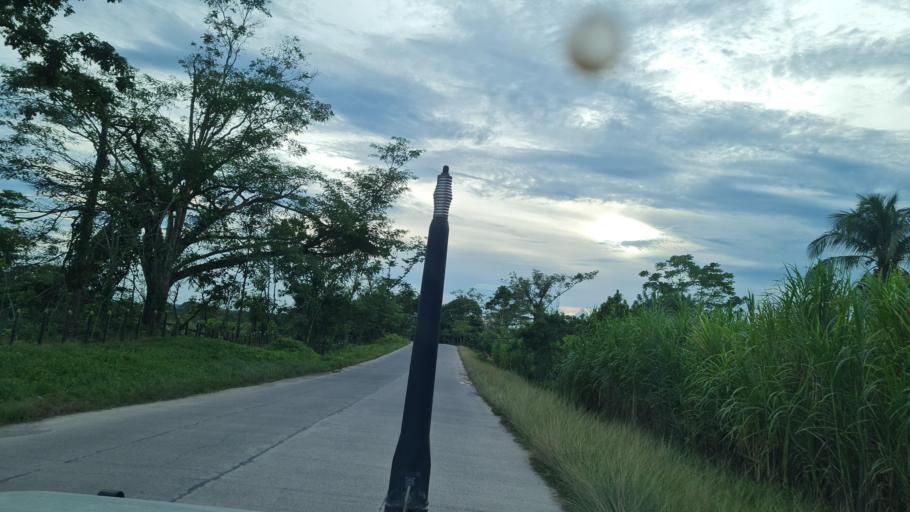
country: NI
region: Atlantico Norte (RAAN)
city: Siuna
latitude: 13.6838
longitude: -84.5905
